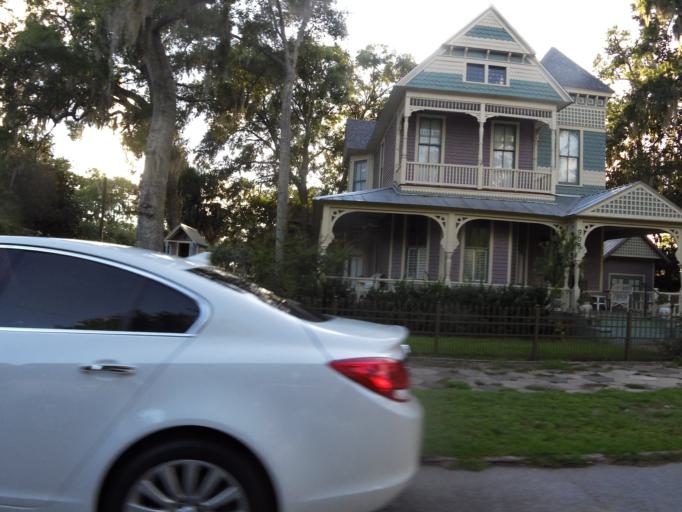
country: US
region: Georgia
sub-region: Glynn County
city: Brunswick
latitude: 31.1417
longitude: -81.4906
